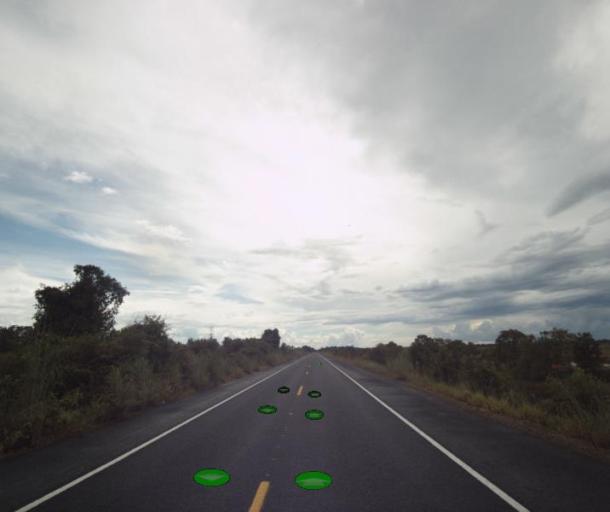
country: BR
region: Goias
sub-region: Sao Miguel Do Araguaia
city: Sao Miguel do Araguaia
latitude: -13.2380
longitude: -50.5488
